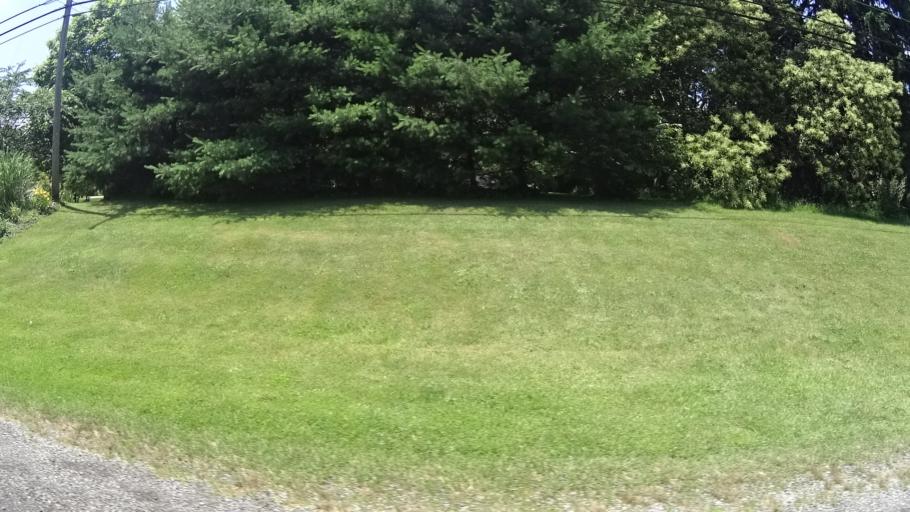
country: US
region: Ohio
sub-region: Lorain County
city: Vermilion
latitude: 41.3605
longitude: -82.3601
